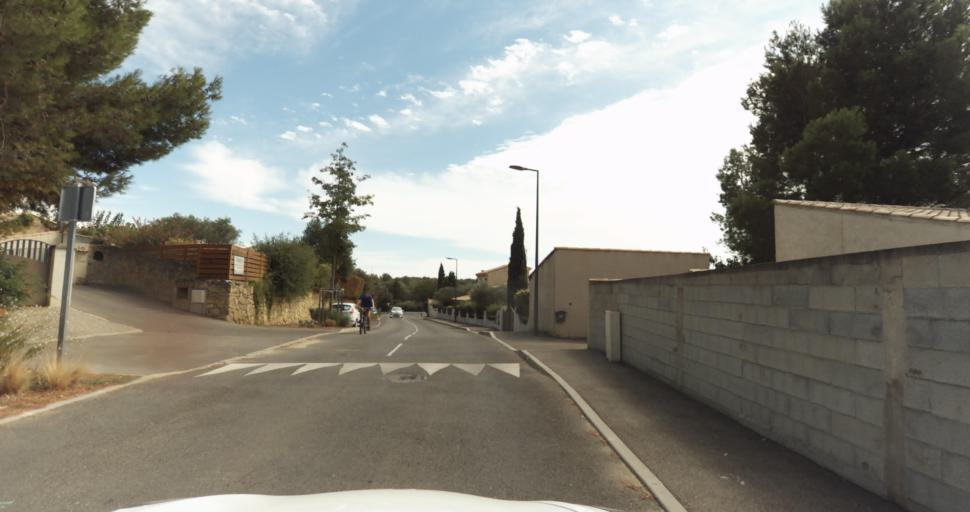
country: FR
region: Provence-Alpes-Cote d'Azur
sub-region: Departement des Bouches-du-Rhone
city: Miramas
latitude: 43.5797
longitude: 5.0237
